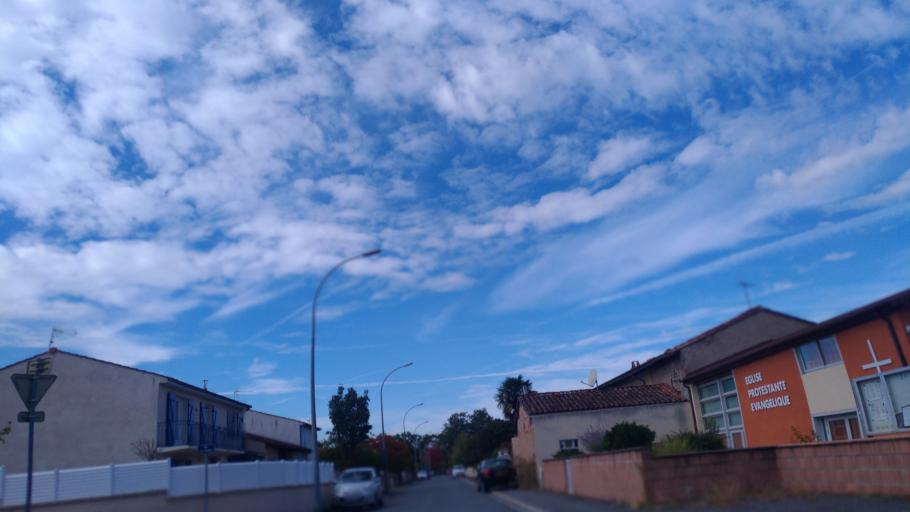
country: FR
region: Midi-Pyrenees
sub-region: Departement du Tarn
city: Puygouzon
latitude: 43.9150
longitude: 2.1717
